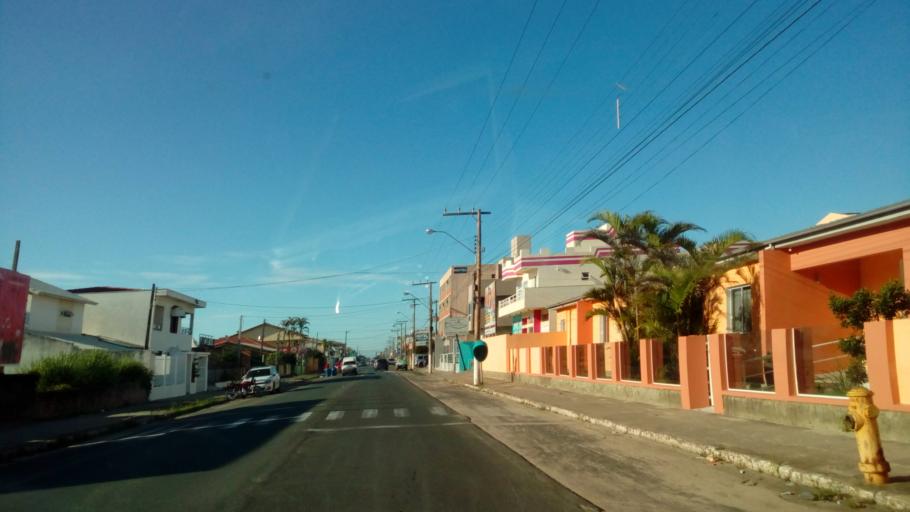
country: BR
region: Santa Catarina
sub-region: Laguna
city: Laguna
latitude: -28.4884
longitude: -48.7706
